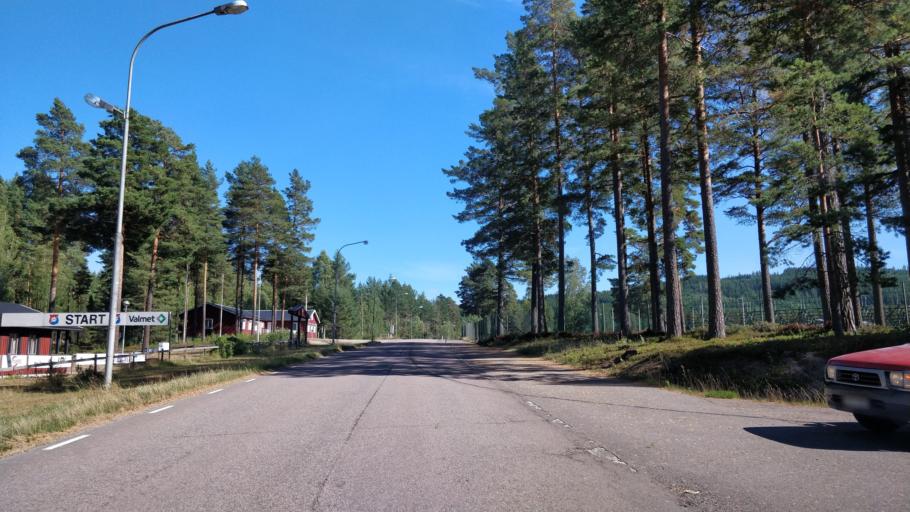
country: SE
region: Vaermland
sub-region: Hagfors Kommun
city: Hagfors
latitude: 60.0409
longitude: 13.7146
